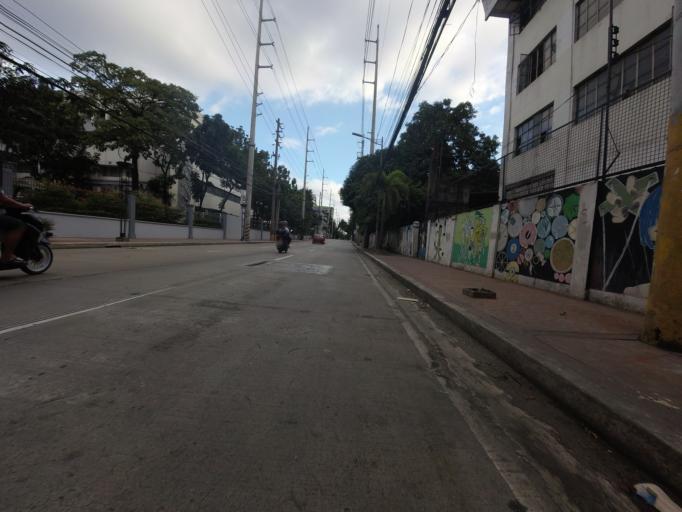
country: PH
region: Metro Manila
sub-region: City of Manila
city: Quiapo
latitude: 14.5873
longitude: 120.9854
